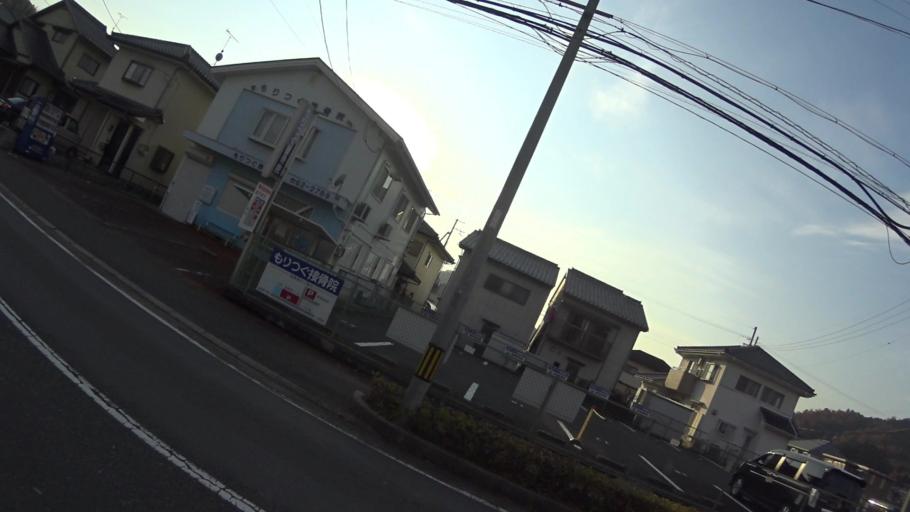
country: JP
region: Kyoto
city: Maizuru
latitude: 35.4834
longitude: 135.4336
